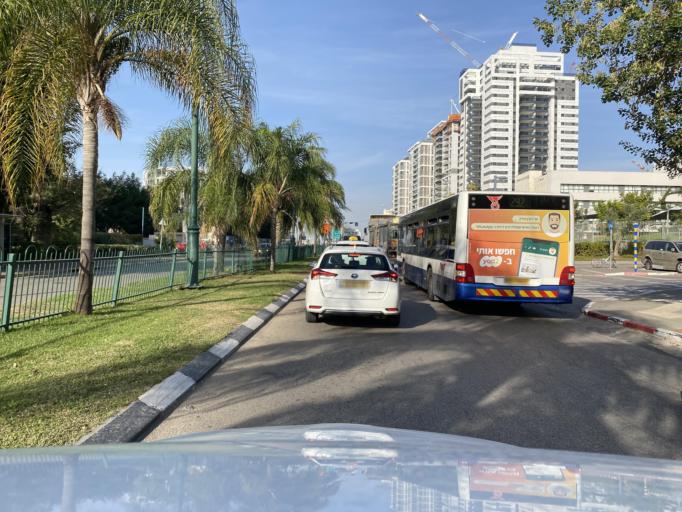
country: IL
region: Tel Aviv
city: Giv`at Shemu'el
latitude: 32.0687
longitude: 34.8501
